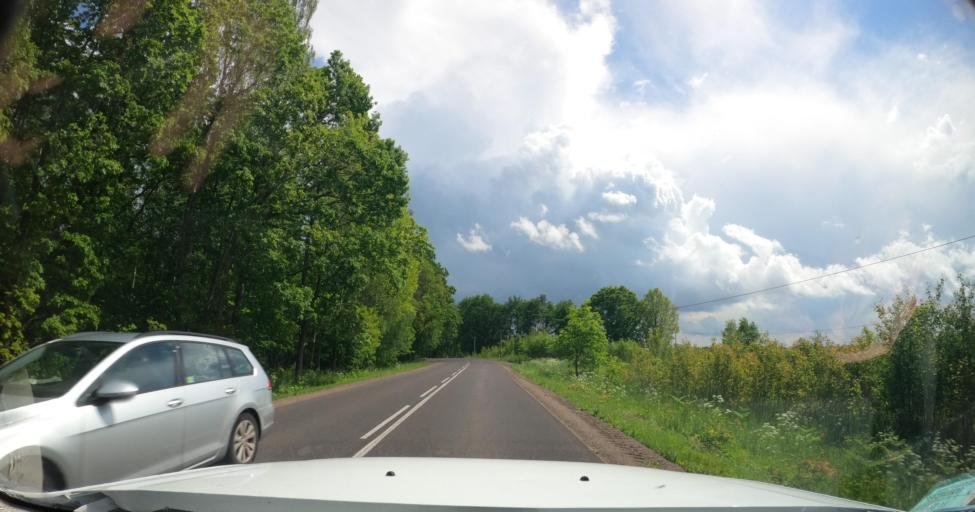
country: PL
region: Pomeranian Voivodeship
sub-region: Powiat bytowski
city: Czarna Dabrowka
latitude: 54.3465
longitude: 17.5847
